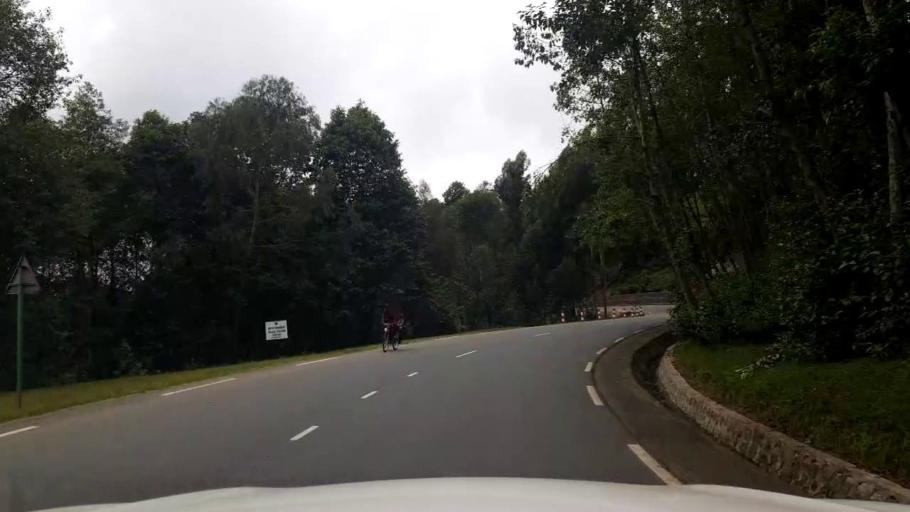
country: RW
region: Northern Province
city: Musanze
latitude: -1.6563
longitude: 29.5094
